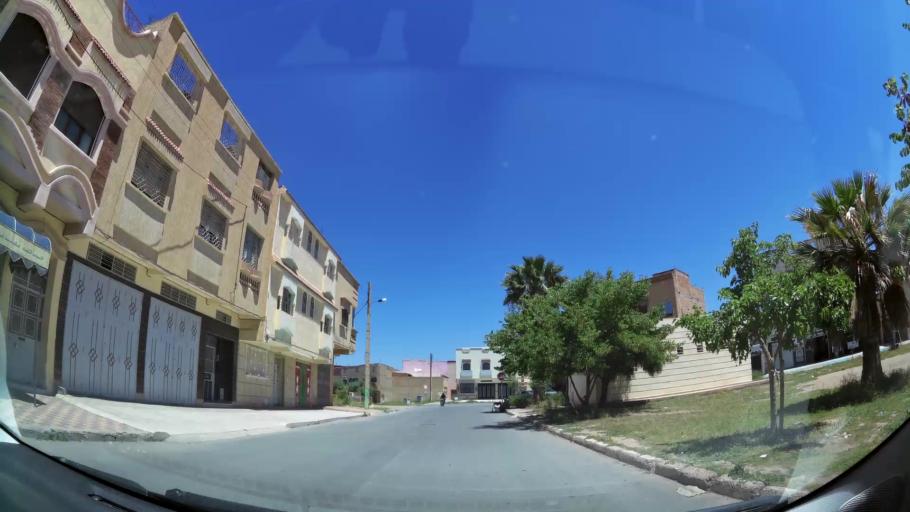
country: MA
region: Oriental
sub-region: Oujda-Angad
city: Oujda
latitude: 34.6792
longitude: -1.8759
